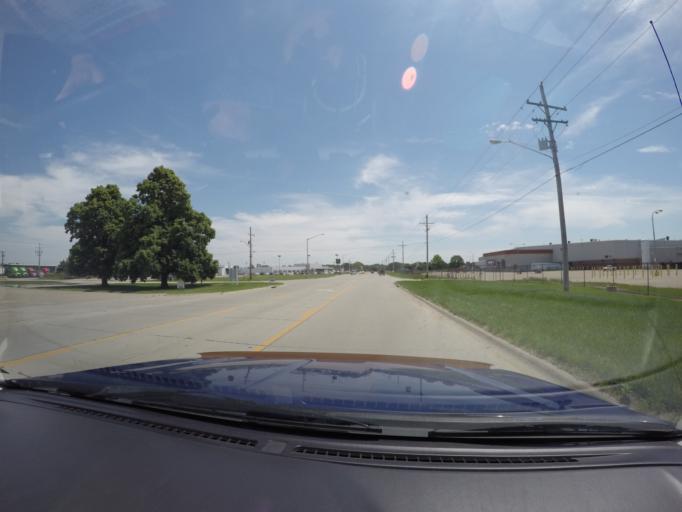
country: US
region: Nebraska
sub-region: Hall County
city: Grand Island
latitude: 40.9024
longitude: -98.3855
